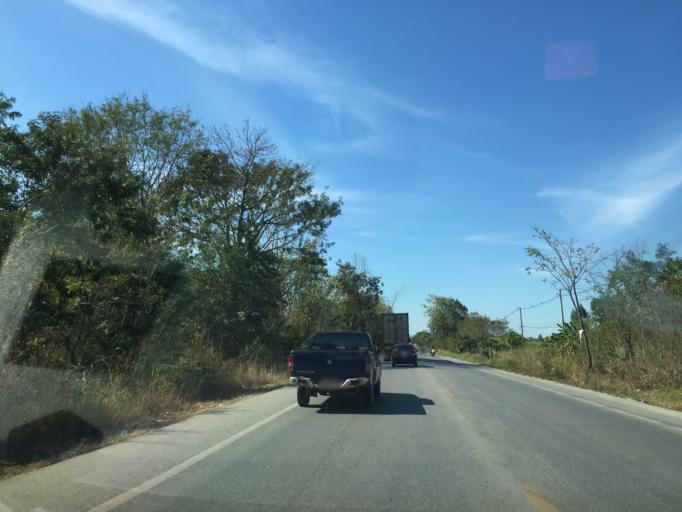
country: TH
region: Changwat Nong Bua Lamphu
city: Na Klang
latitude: 17.3136
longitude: 102.1674
